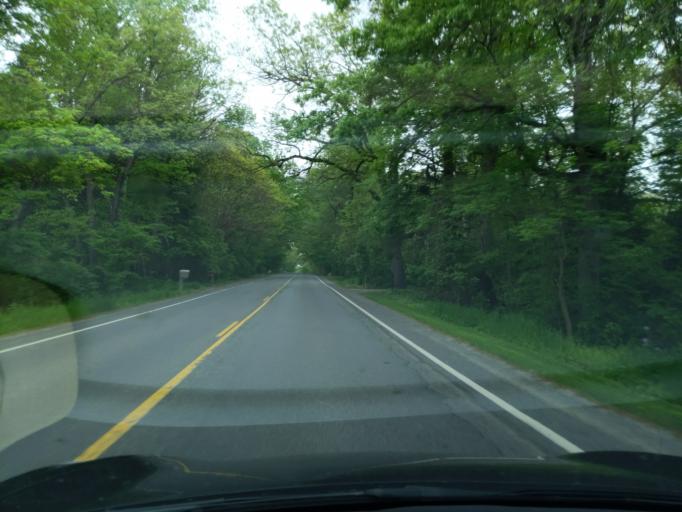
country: US
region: Michigan
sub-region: Ingham County
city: Haslett
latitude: 42.7193
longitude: -84.3635
